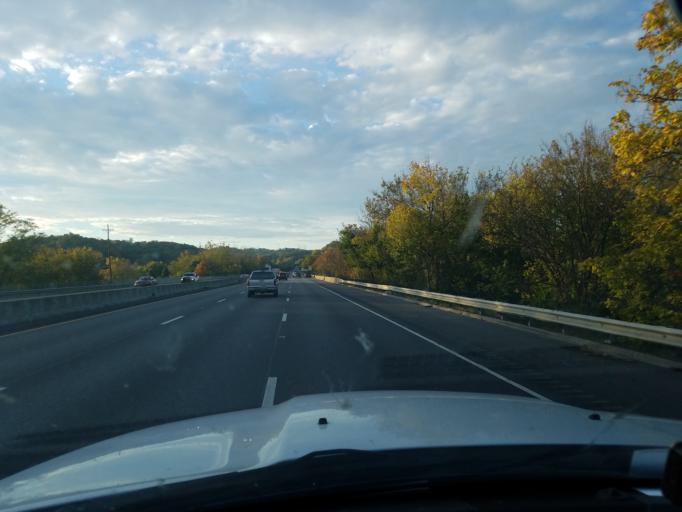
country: US
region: Indiana
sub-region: Floyd County
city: New Albany
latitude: 38.2899
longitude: -85.8341
